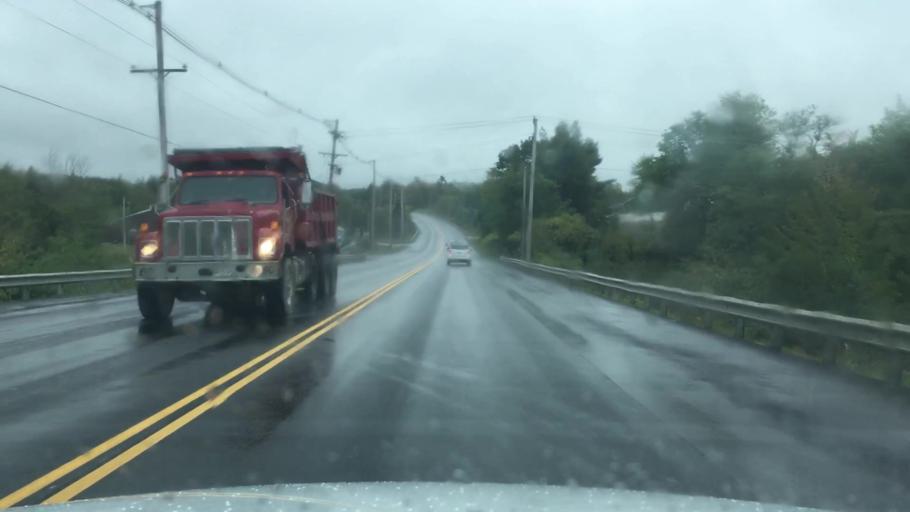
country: US
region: Maine
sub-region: Penobscot County
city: Hampden
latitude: 44.7709
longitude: -68.8574
